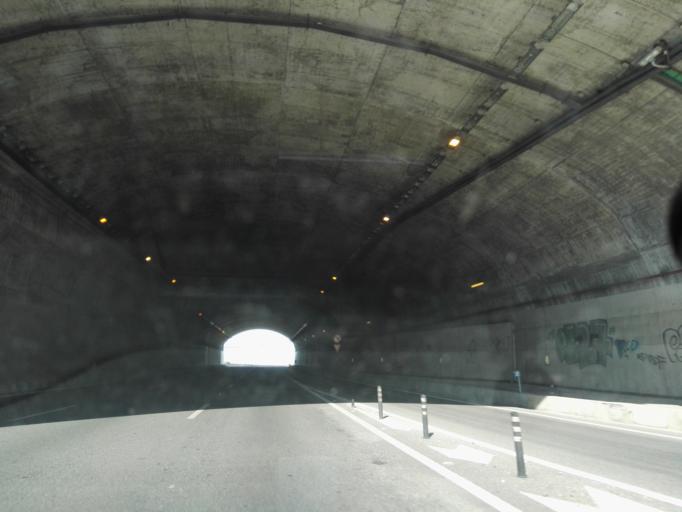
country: PT
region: Lisbon
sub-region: Odivelas
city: Olival do Basto
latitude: 38.7852
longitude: -9.1541
